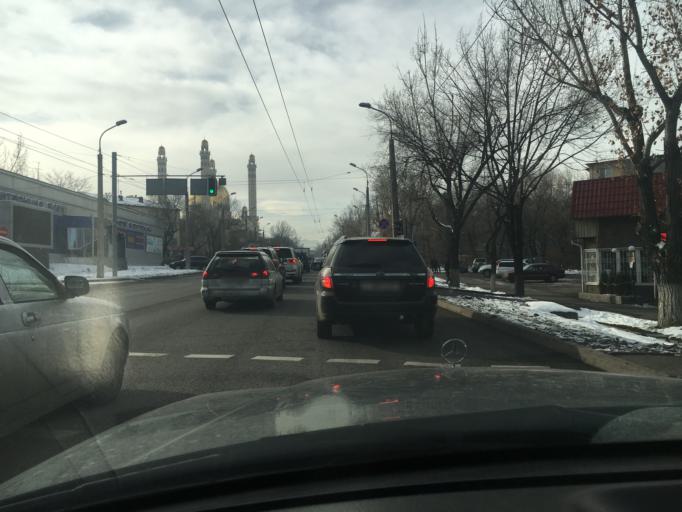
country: KZ
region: Almaty Qalasy
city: Almaty
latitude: 43.2295
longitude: 76.8940
